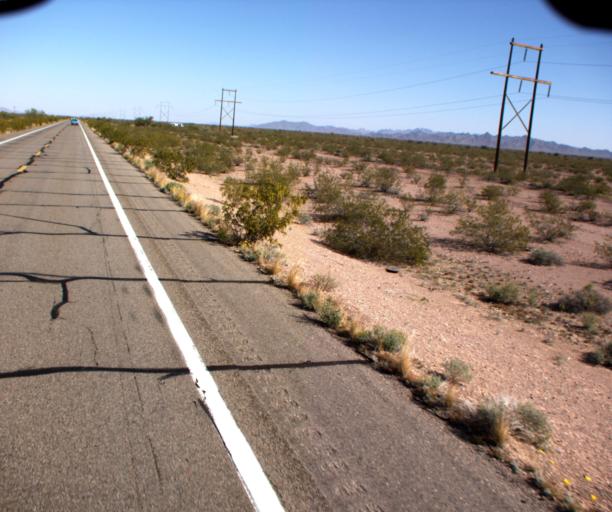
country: US
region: Arizona
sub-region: La Paz County
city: Quartzsite
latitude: 33.3838
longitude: -114.2171
